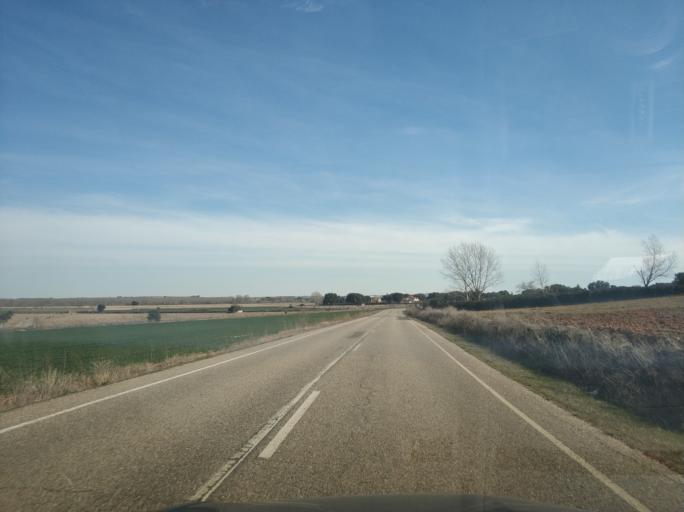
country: ES
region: Castille and Leon
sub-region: Provincia de Salamanca
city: Florida de Liebana
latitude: 41.0233
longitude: -5.7509
